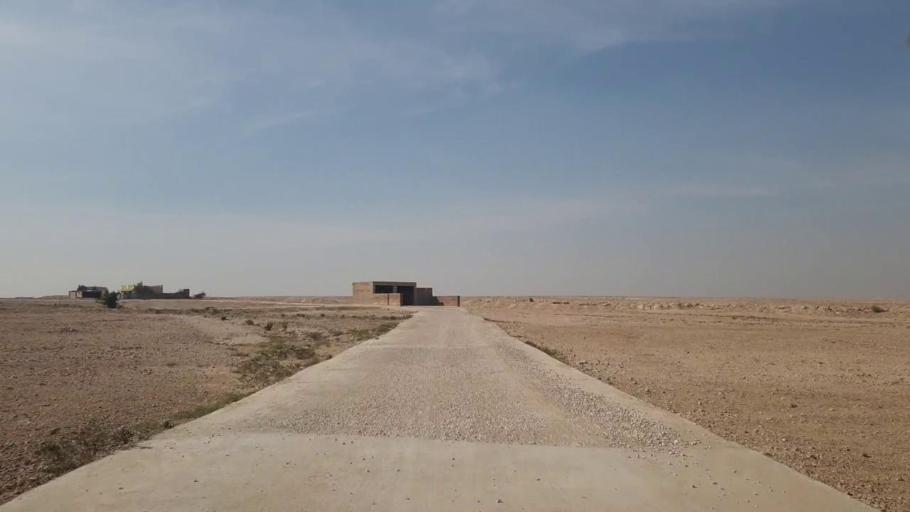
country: PK
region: Sindh
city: Hala
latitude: 25.7804
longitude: 68.2771
